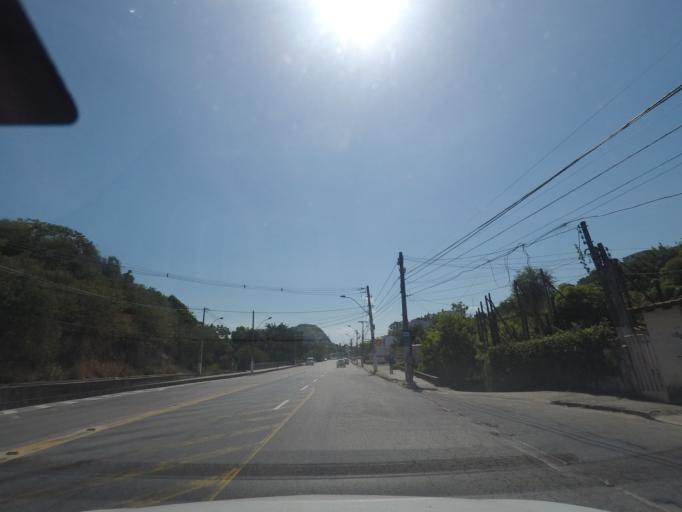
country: BR
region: Rio de Janeiro
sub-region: Niteroi
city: Niteroi
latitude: -22.9113
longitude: -43.0563
